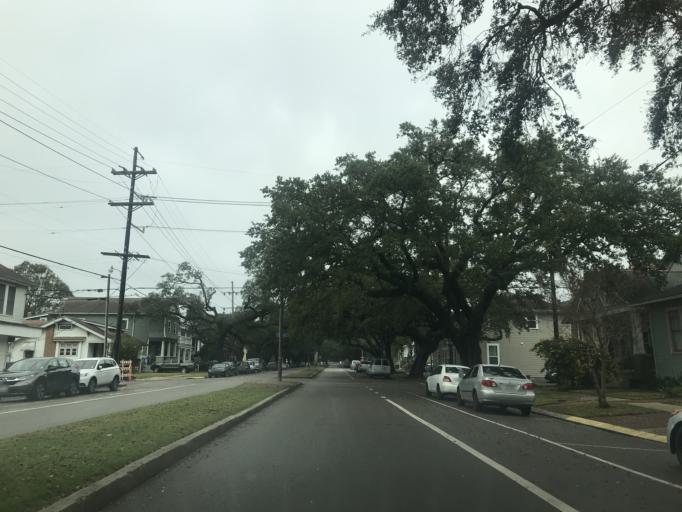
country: US
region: Louisiana
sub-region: Orleans Parish
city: New Orleans
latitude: 29.9746
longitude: -90.1070
